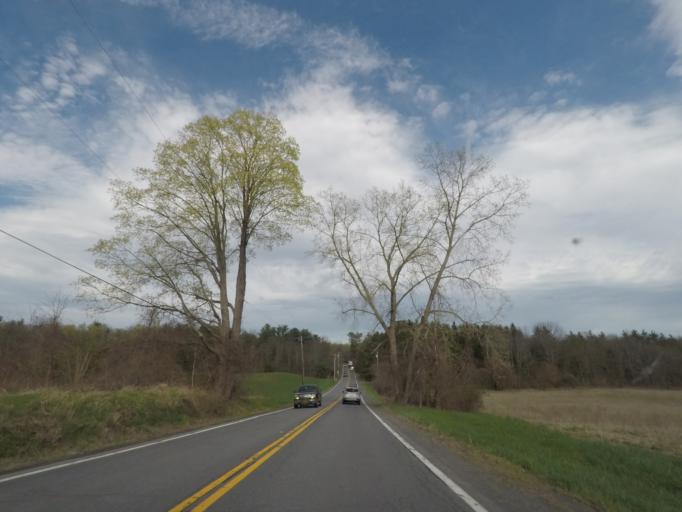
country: US
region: New York
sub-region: Albany County
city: Delmar
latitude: 42.5685
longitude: -73.9025
